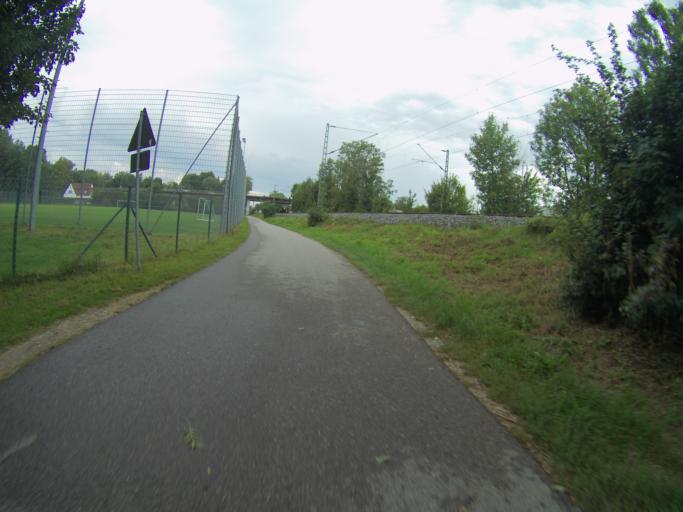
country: DE
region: Bavaria
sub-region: Upper Bavaria
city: Freising
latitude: 48.4017
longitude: 11.7535
